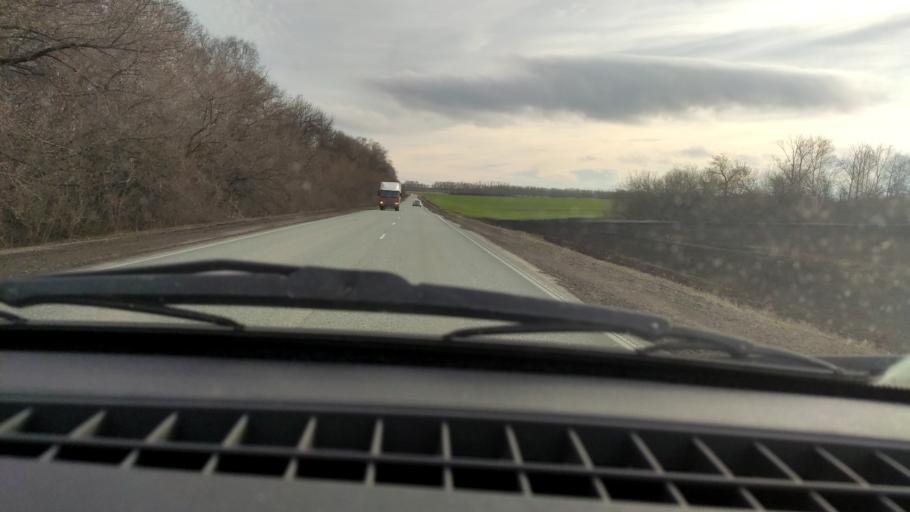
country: RU
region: Bashkortostan
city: Chishmy
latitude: 54.5005
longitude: 55.2840
